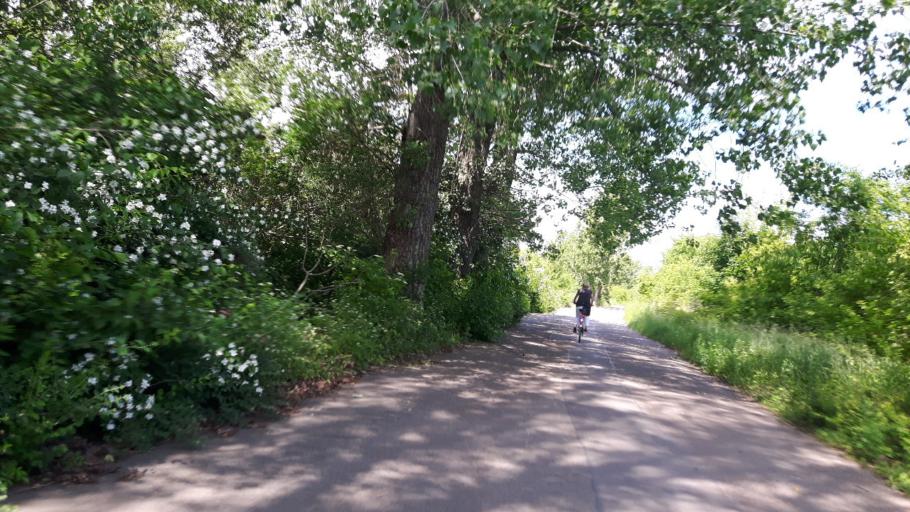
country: DE
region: Saxony
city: Markranstadt
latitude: 51.3084
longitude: 12.2603
